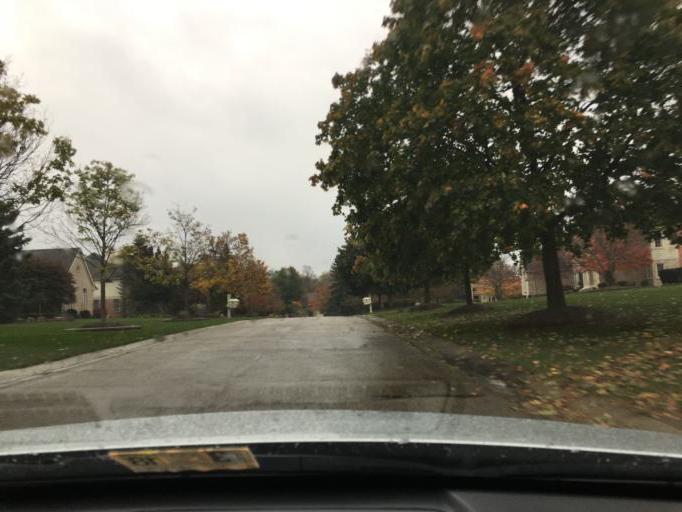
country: US
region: Michigan
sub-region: Oakland County
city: Auburn Hills
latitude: 42.7130
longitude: -83.2038
